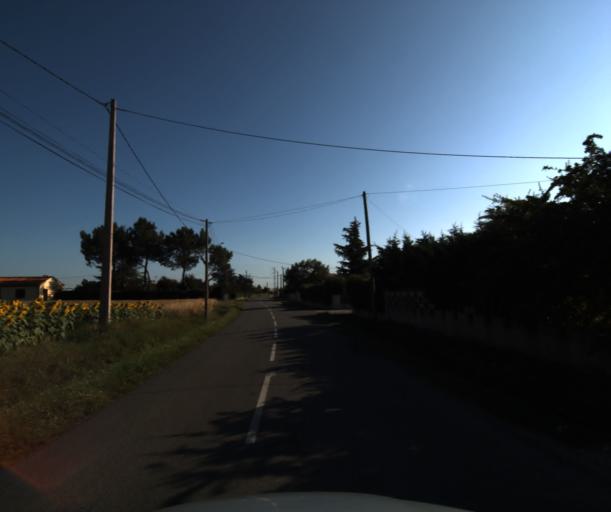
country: FR
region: Midi-Pyrenees
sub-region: Departement de la Haute-Garonne
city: Muret
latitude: 43.4449
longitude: 1.3653
